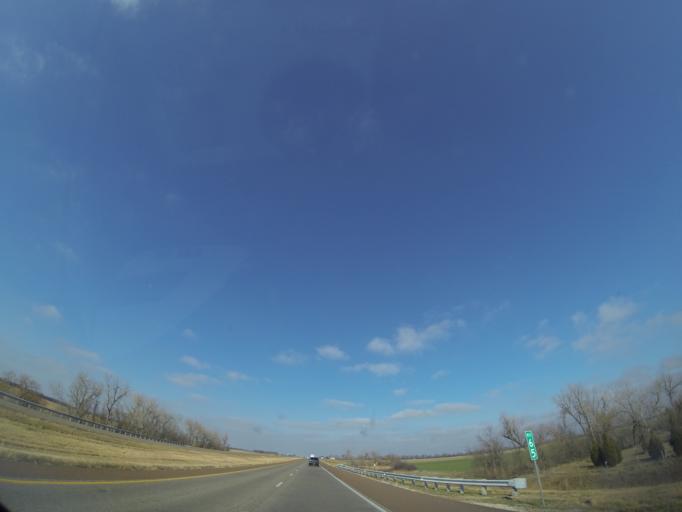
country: US
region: Kansas
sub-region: McPherson County
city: McPherson
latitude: 38.4357
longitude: -97.6207
